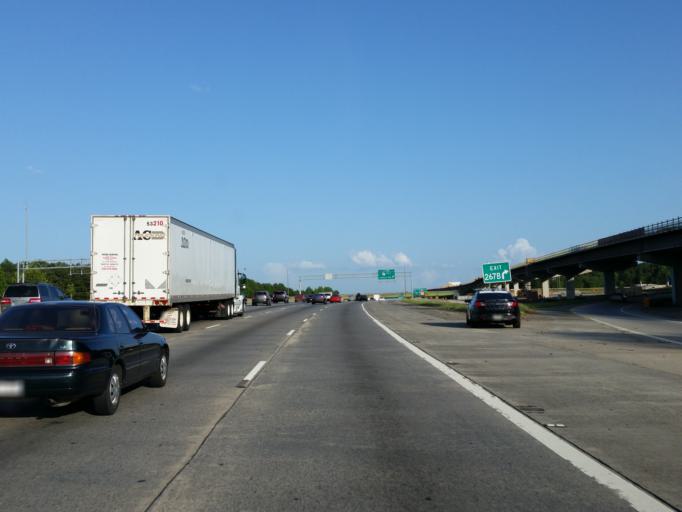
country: US
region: Georgia
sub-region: Cobb County
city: Marietta
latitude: 33.9876
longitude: -84.5456
